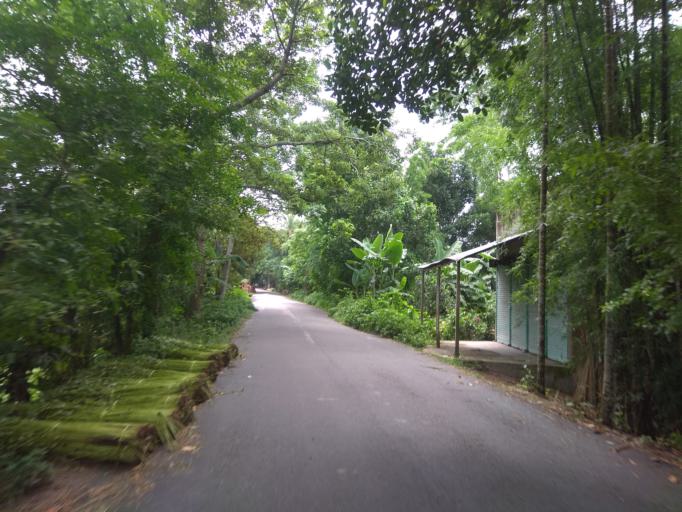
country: BD
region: Dhaka
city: Dohar
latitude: 23.4425
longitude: 90.0667
